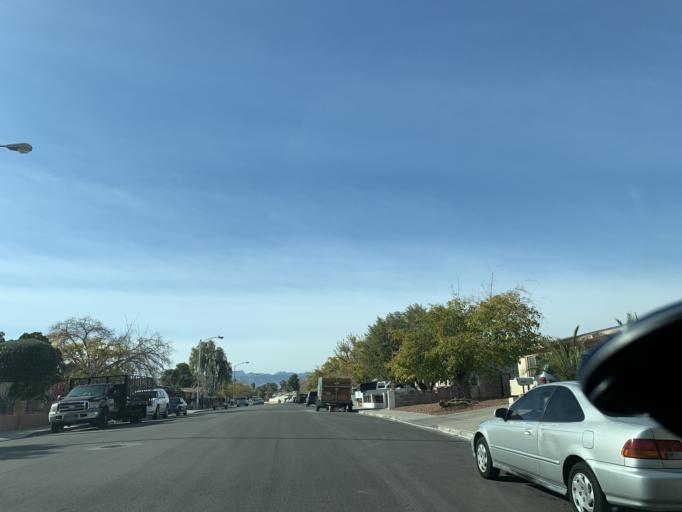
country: US
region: Nevada
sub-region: Clark County
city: Spring Valley
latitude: 36.1105
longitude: -115.2272
